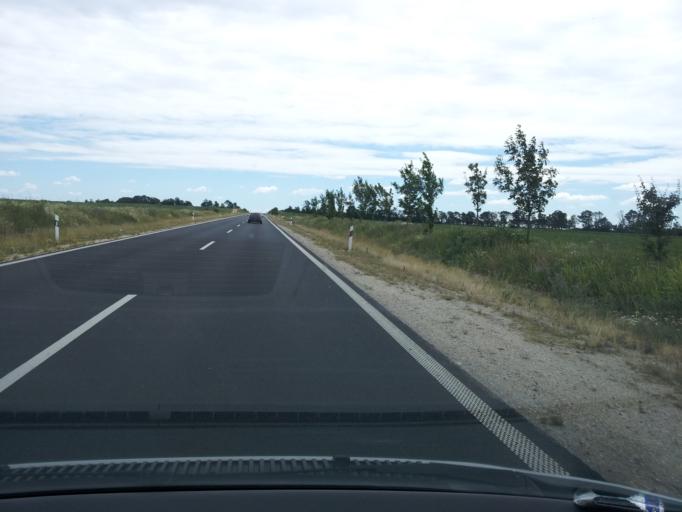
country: HU
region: Veszprem
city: Balatonkenese
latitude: 47.0643
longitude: 18.0870
